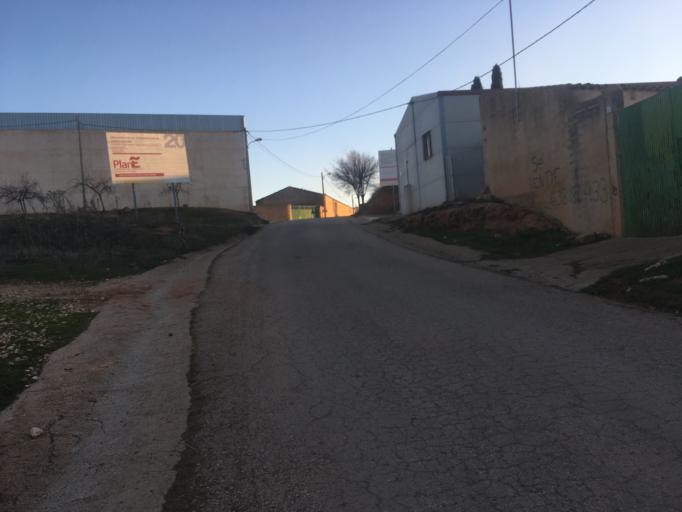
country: ES
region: Castille-La Mancha
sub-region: Provincia de Cuenca
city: Atalaya del Canavate
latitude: 39.5515
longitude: -2.2520
